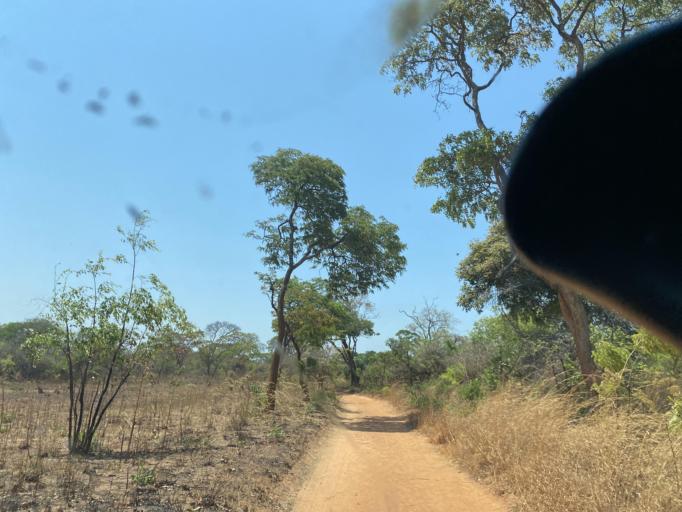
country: ZM
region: Lusaka
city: Chongwe
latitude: -15.4245
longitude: 29.1798
